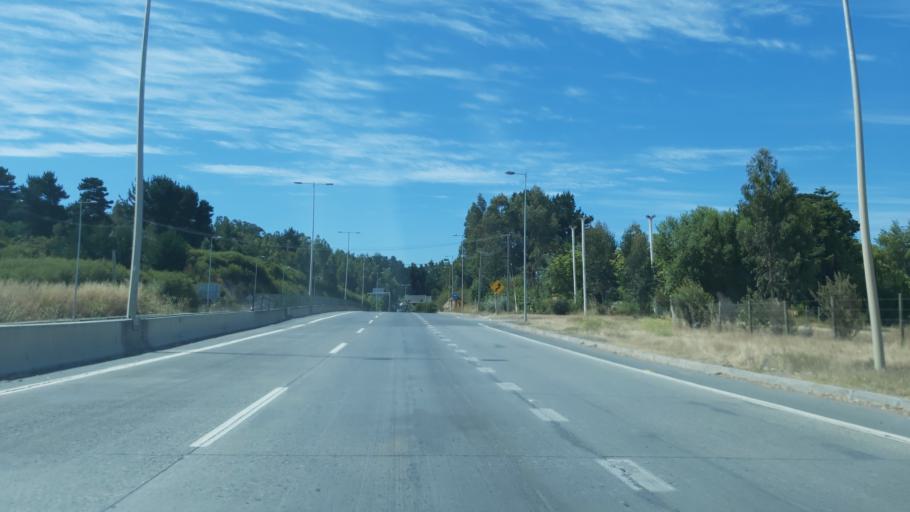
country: CL
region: Biobio
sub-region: Provincia de Concepcion
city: Coronel
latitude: -37.0488
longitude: -73.1420
